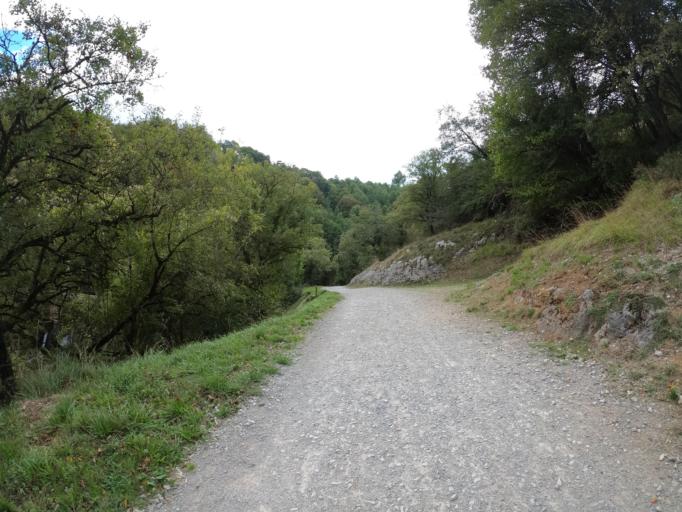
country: ES
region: Navarre
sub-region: Provincia de Navarra
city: Lekunberri
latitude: 42.9893
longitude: -1.8868
